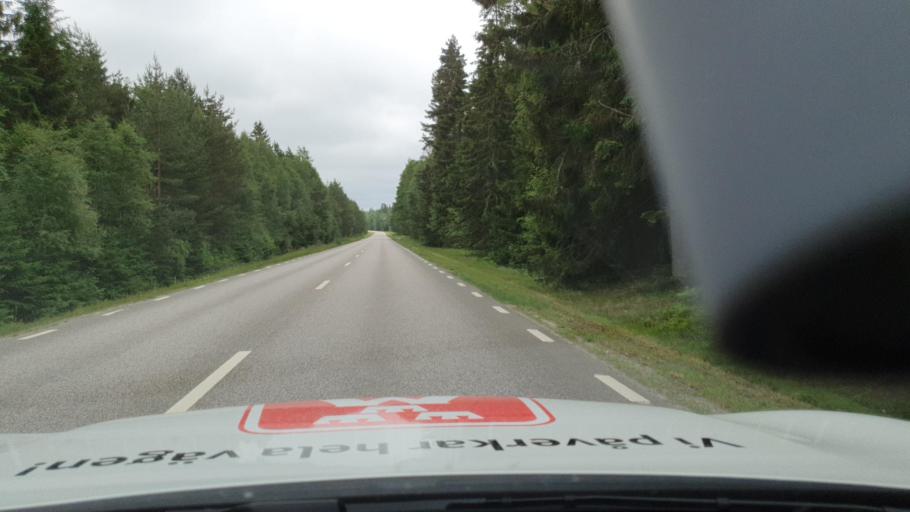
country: SE
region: Vaestra Goetaland
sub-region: Tibro Kommun
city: Tibro
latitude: 58.3731
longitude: 14.2044
